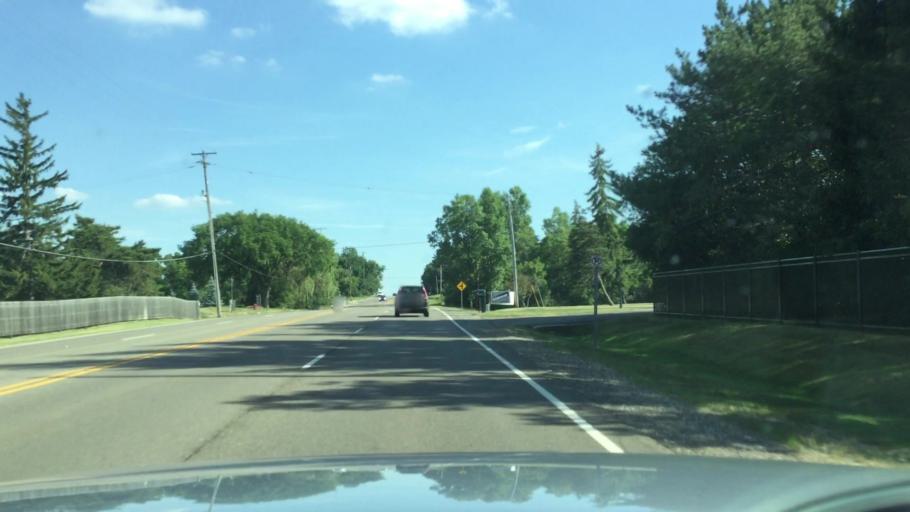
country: US
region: Michigan
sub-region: Genesee County
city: Grand Blanc
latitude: 42.9003
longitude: -83.6021
